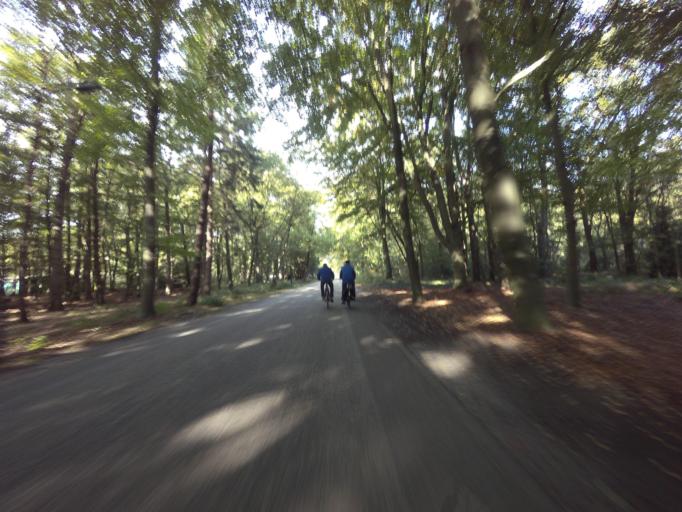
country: NL
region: North Holland
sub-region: Gemeente Wijdemeren
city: Nieuw-Loosdrecht
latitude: 52.2072
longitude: 5.1467
